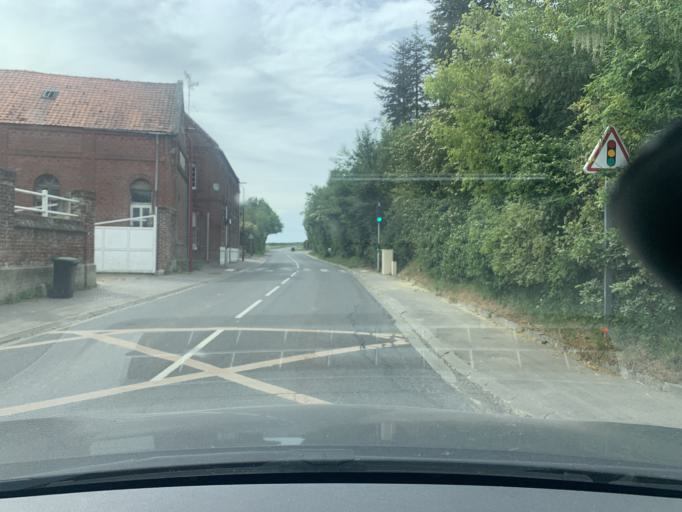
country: FR
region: Nord-Pas-de-Calais
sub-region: Departement du Nord
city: Marcoing
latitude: 50.1356
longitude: 3.1825
